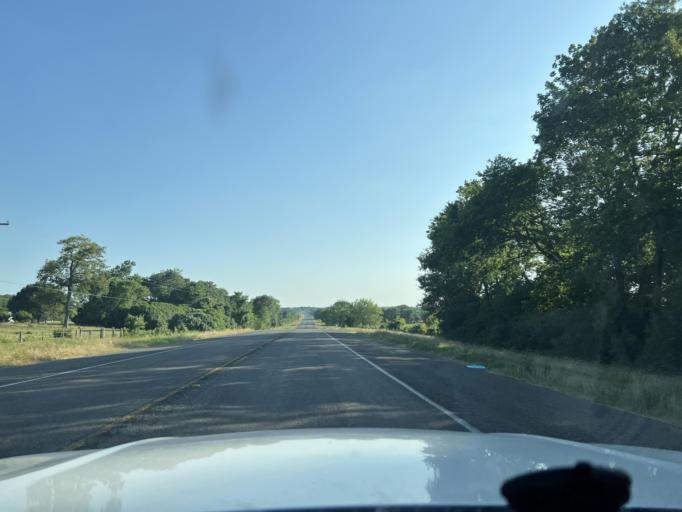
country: US
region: Texas
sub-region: Washington County
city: Brenham
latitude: 30.2316
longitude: -96.2901
